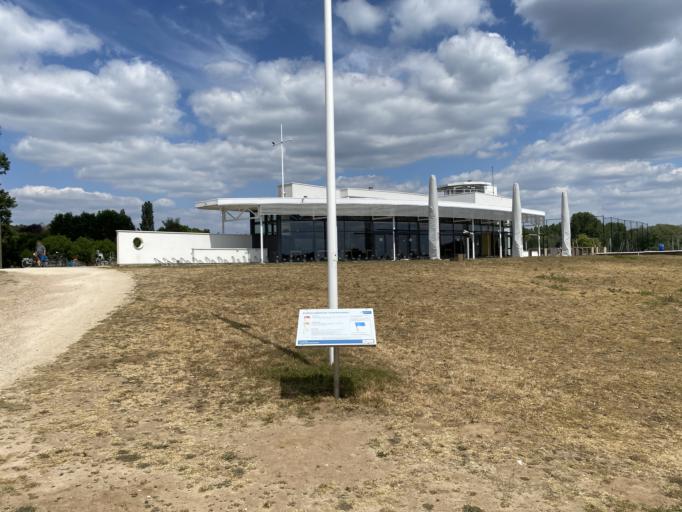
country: BE
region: Flanders
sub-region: Provincie Limburg
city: Herk-de-Stad
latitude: 50.9628
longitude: 5.1462
